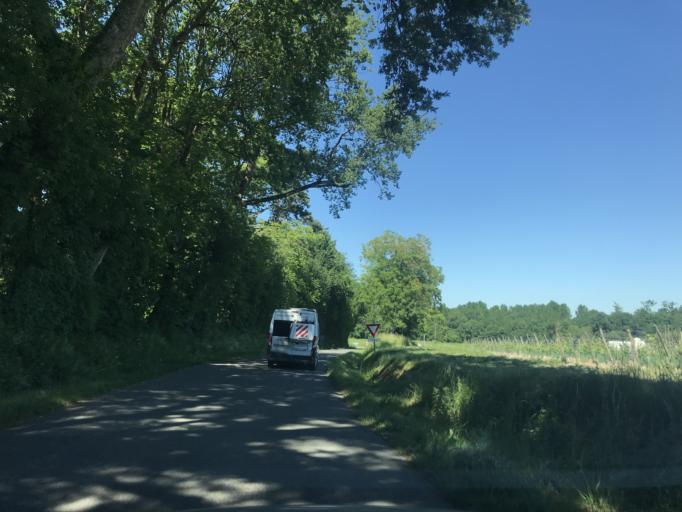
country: FR
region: Poitou-Charentes
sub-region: Departement de la Charente-Maritime
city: Mortagne-sur-Gironde
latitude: 45.4264
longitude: -0.7088
